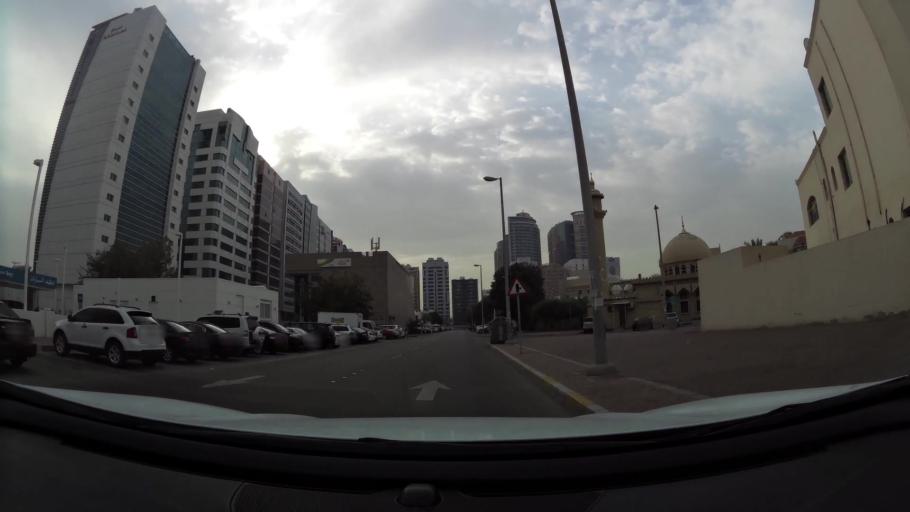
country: AE
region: Abu Dhabi
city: Abu Dhabi
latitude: 24.4762
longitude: 54.3713
